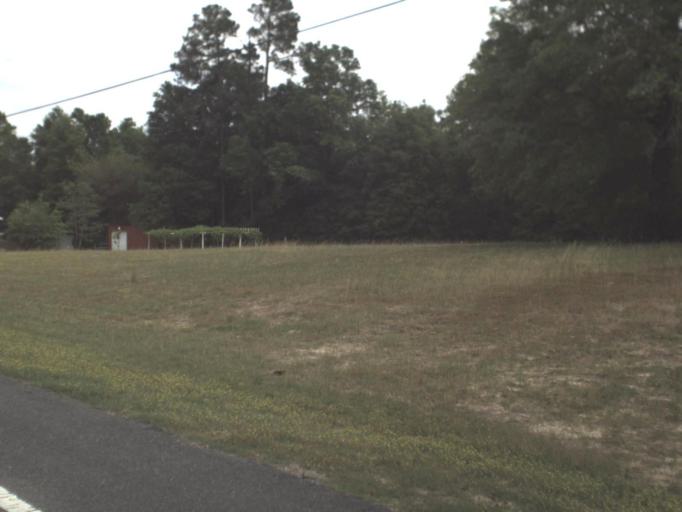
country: US
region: Florida
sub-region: Santa Rosa County
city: Point Baker
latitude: 30.6982
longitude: -87.0669
